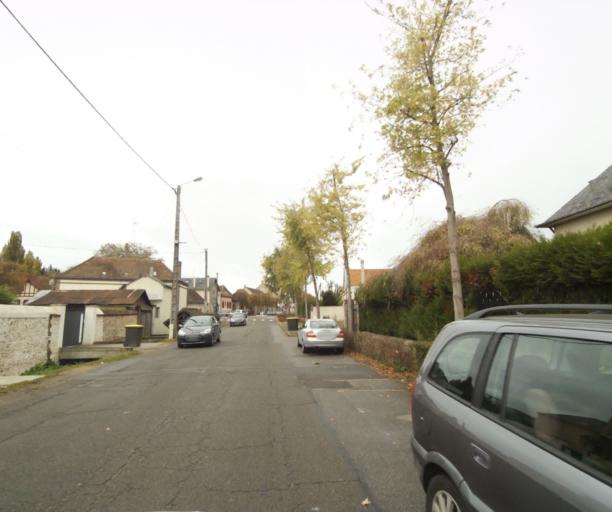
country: FR
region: Centre
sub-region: Departement d'Eure-et-Loir
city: Dreux
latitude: 48.7411
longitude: 1.3775
